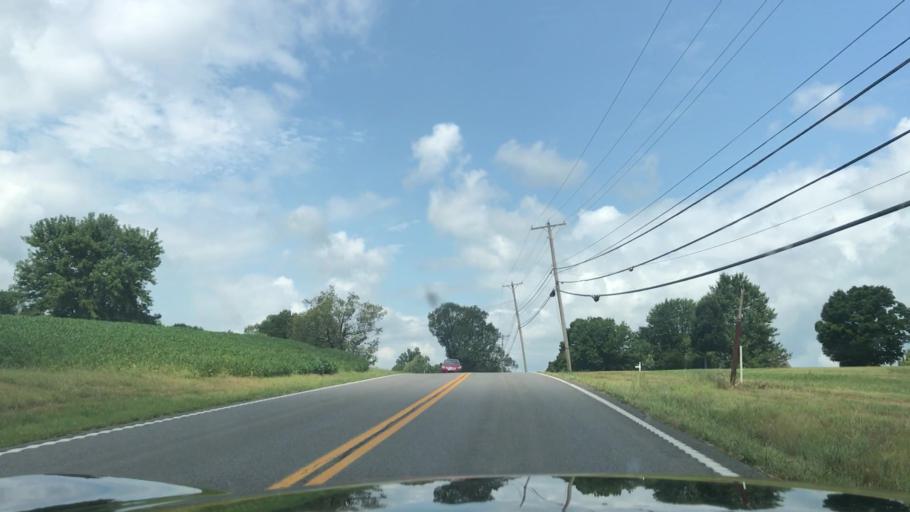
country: US
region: Kentucky
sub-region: Muhlenberg County
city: Greenville
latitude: 37.2048
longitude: -87.1458
